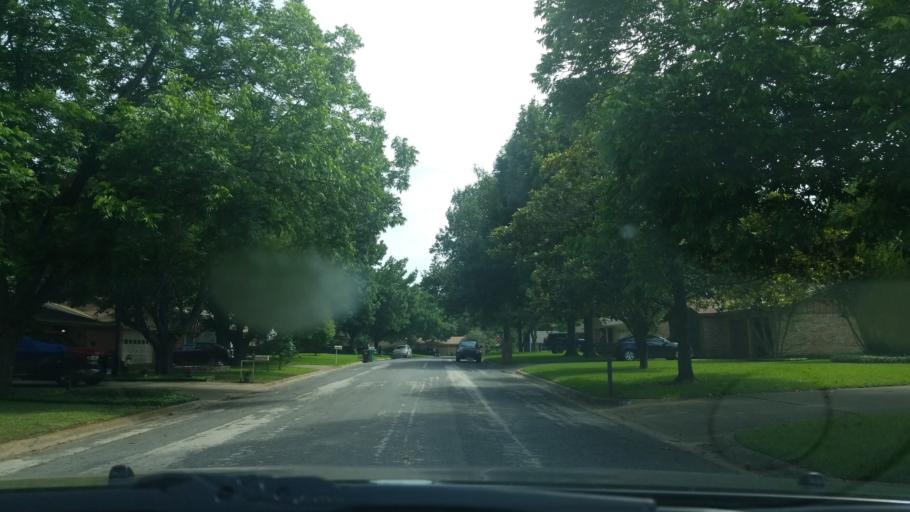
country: US
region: Texas
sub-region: Denton County
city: Denton
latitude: 33.2344
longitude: -97.1494
